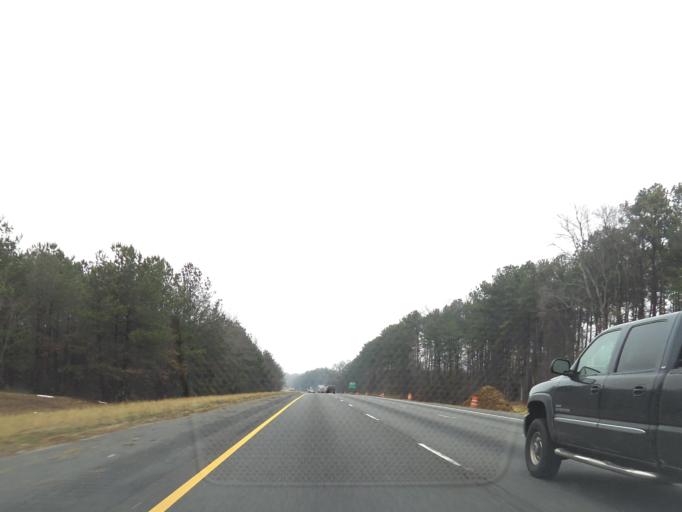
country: US
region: Georgia
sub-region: Henry County
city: McDonough
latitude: 33.3905
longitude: -84.1451
